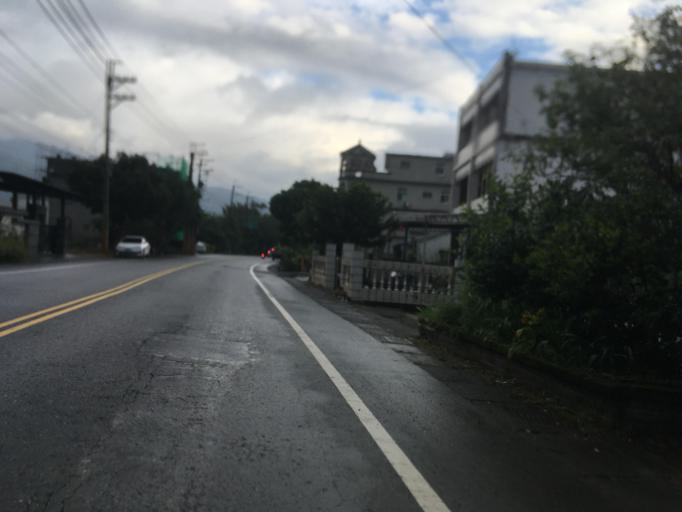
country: TW
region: Taiwan
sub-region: Yilan
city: Yilan
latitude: 24.8333
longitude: 121.8032
